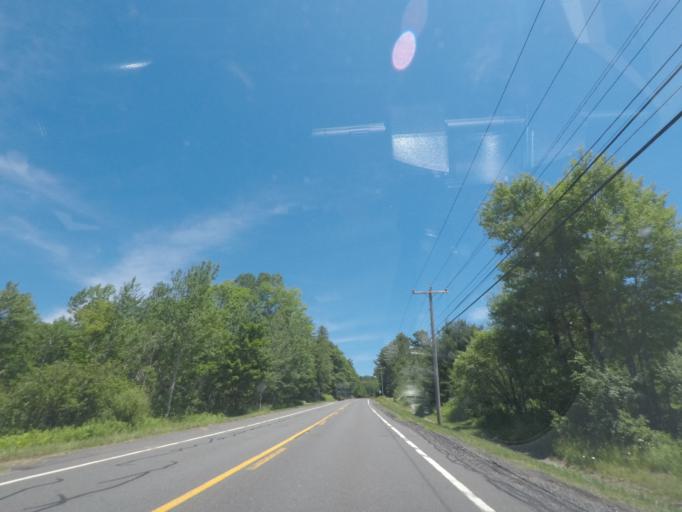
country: US
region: Massachusetts
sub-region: Berkshire County
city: Otis
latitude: 42.2596
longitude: -73.0994
